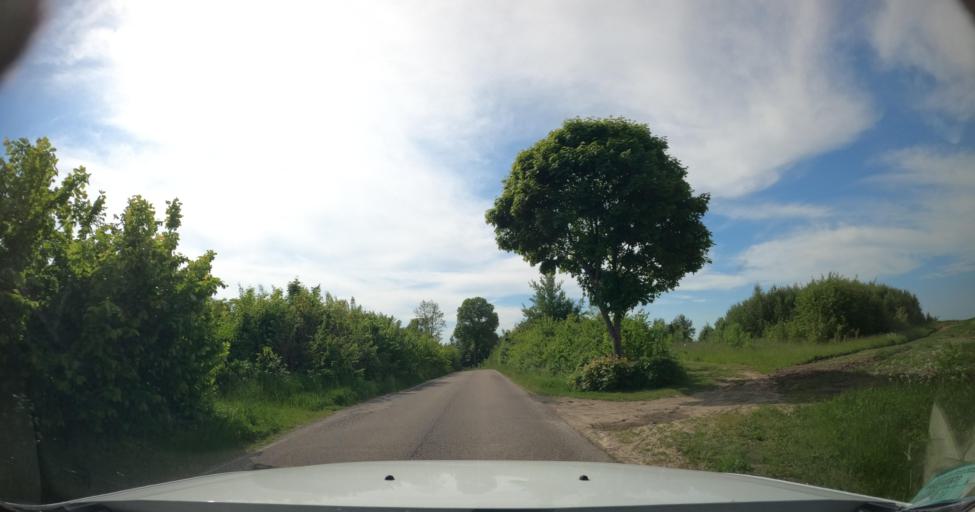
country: PL
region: Warmian-Masurian Voivodeship
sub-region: Powiat ostrodzki
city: Milakowo
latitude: 54.0091
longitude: 20.1334
